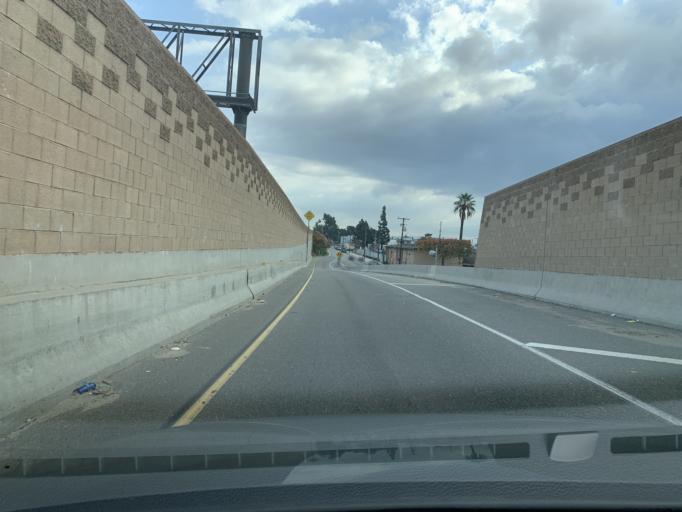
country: US
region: California
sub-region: Los Angeles County
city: El Monte
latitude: 34.0677
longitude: -118.0340
